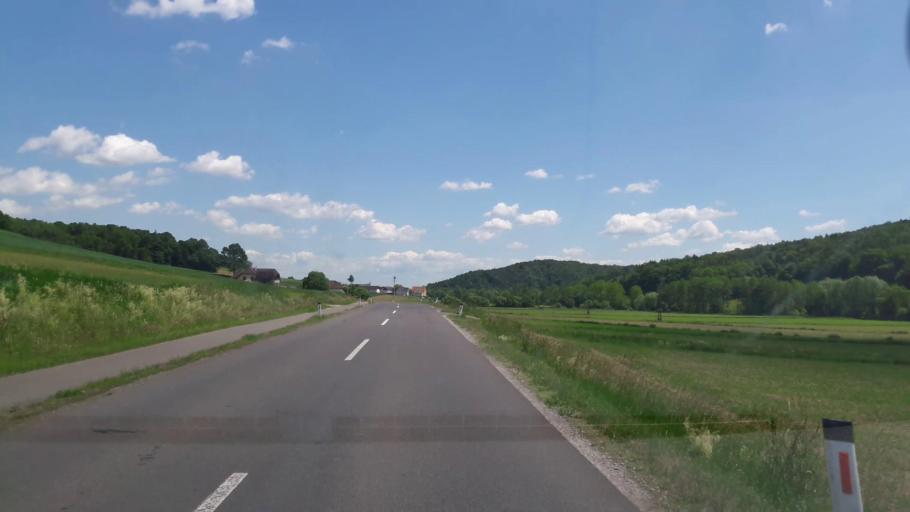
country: AT
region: Styria
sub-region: Politischer Bezirk Suedoststeiermark
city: Unterlamm
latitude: 46.9655
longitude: 16.0842
